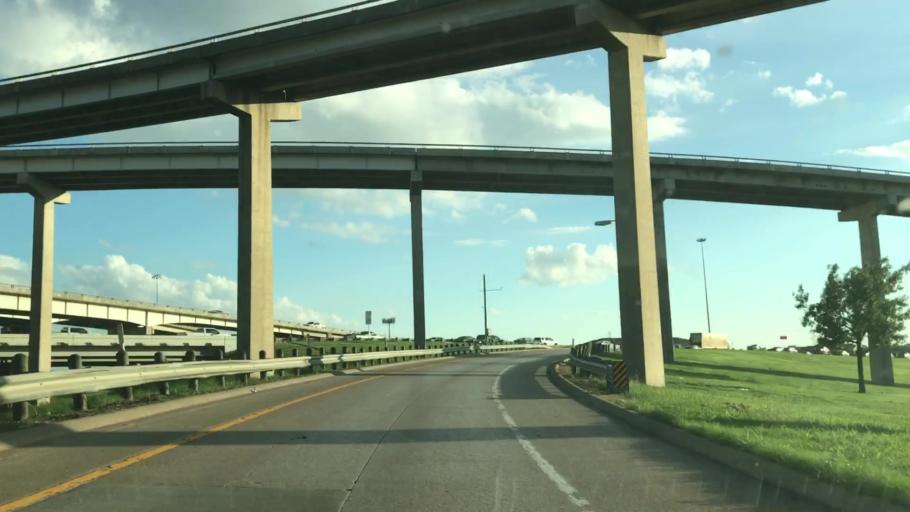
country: US
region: Texas
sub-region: Dallas County
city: Mesquite
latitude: 32.8239
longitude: -96.6303
